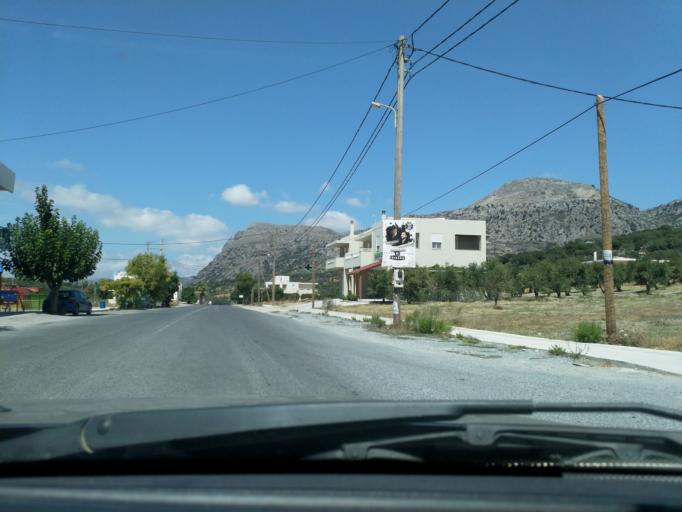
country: GR
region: Crete
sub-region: Nomos Rethymnis
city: Agia Foteini
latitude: 35.1875
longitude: 24.5542
